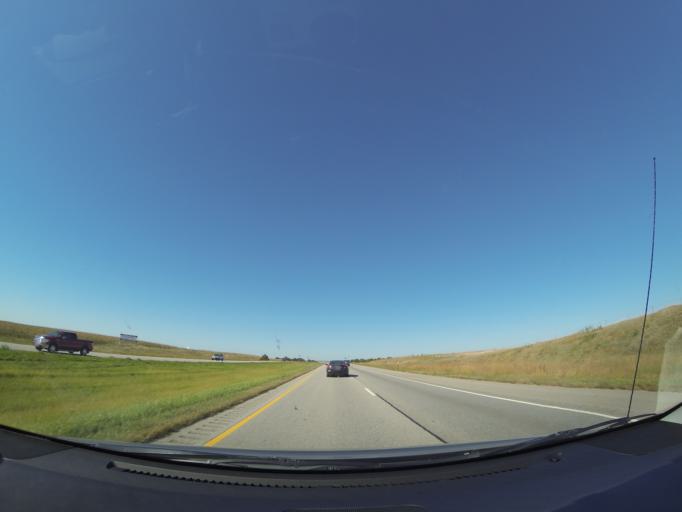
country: US
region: Nebraska
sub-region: Seward County
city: Milford
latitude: 40.8223
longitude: -97.0929
